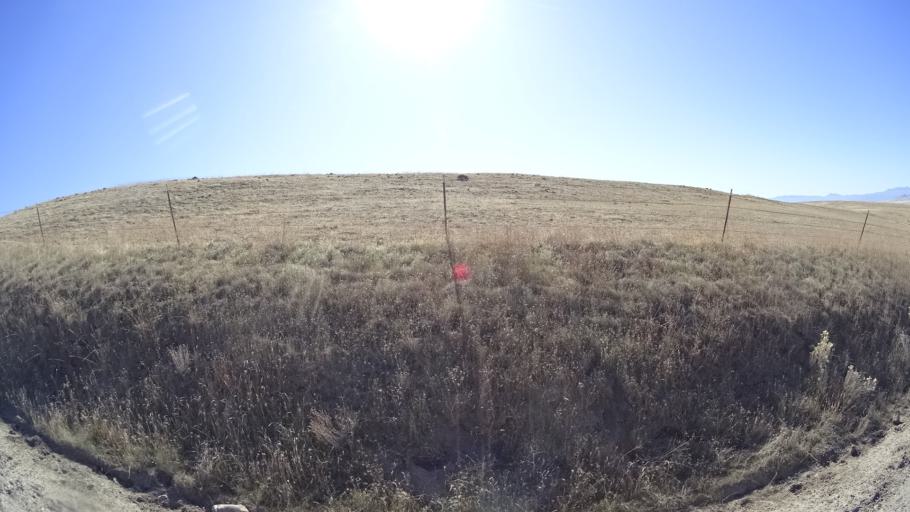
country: US
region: California
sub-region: Siskiyou County
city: Montague
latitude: 41.8298
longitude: -122.4033
